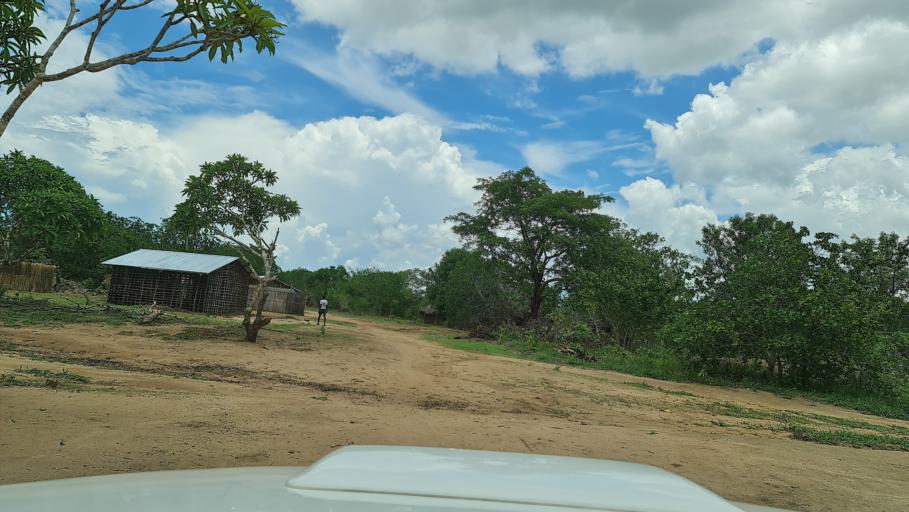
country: MZ
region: Nampula
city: Ilha de Mocambique
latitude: -15.5152
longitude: 40.2029
